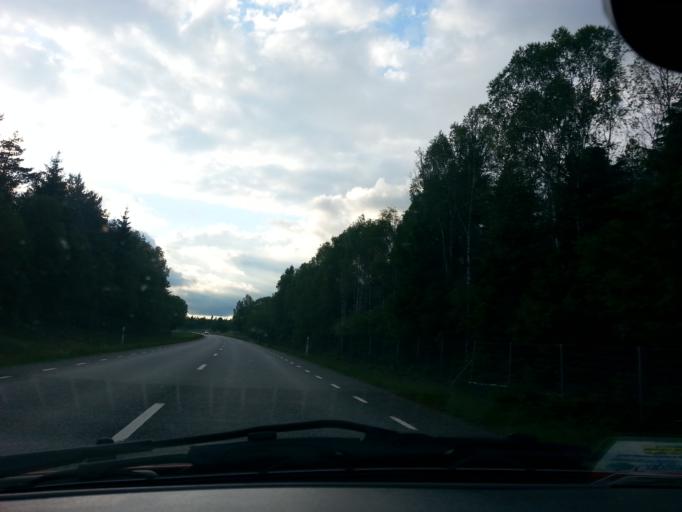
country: SE
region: Vaestra Goetaland
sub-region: Tranemo Kommun
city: Limmared
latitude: 57.5430
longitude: 13.3326
